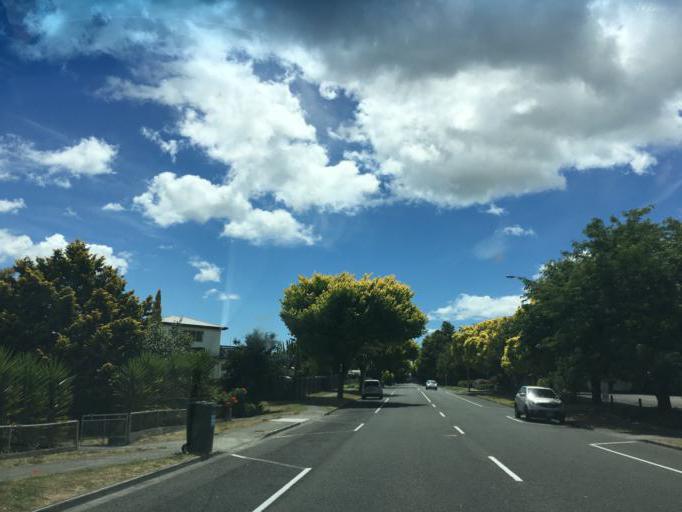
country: NZ
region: Hawke's Bay
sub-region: Hastings District
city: Hastings
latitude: -39.6453
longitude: 176.8580
